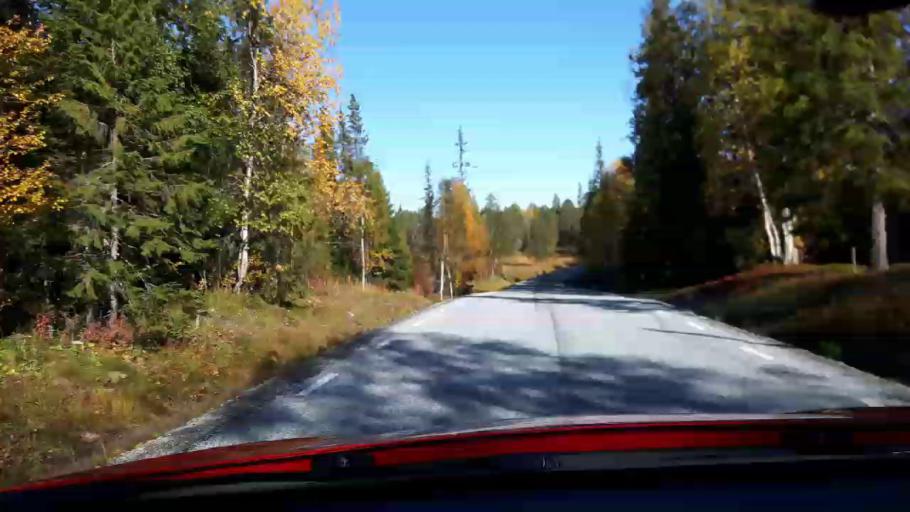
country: NO
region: Nord-Trondelag
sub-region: Royrvik
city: Royrvik
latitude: 64.8180
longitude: 14.2202
